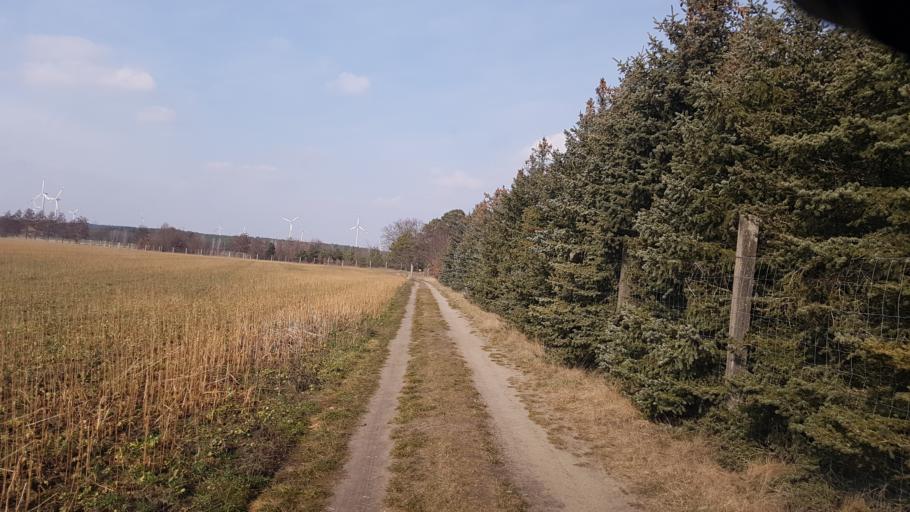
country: DE
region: Brandenburg
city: Schilda
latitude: 51.6352
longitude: 13.3794
